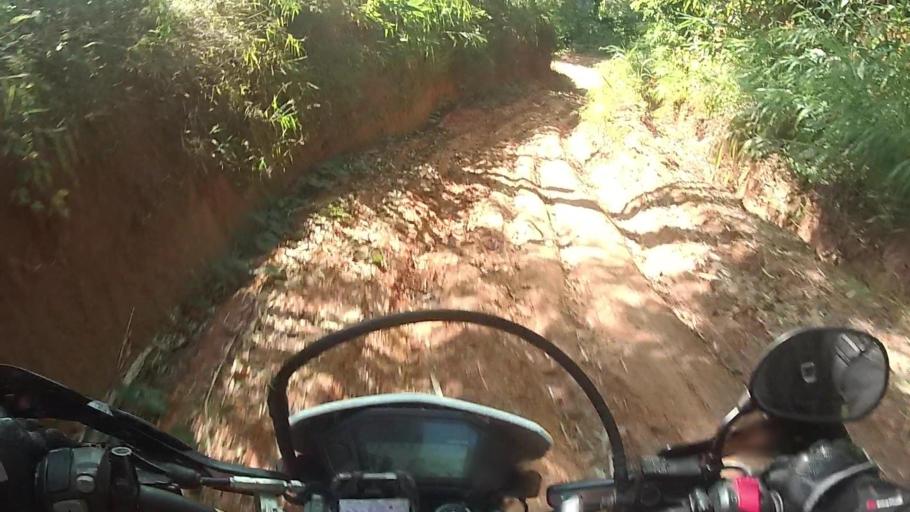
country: TH
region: Chiang Mai
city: Phrao
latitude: 19.3975
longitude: 99.3009
